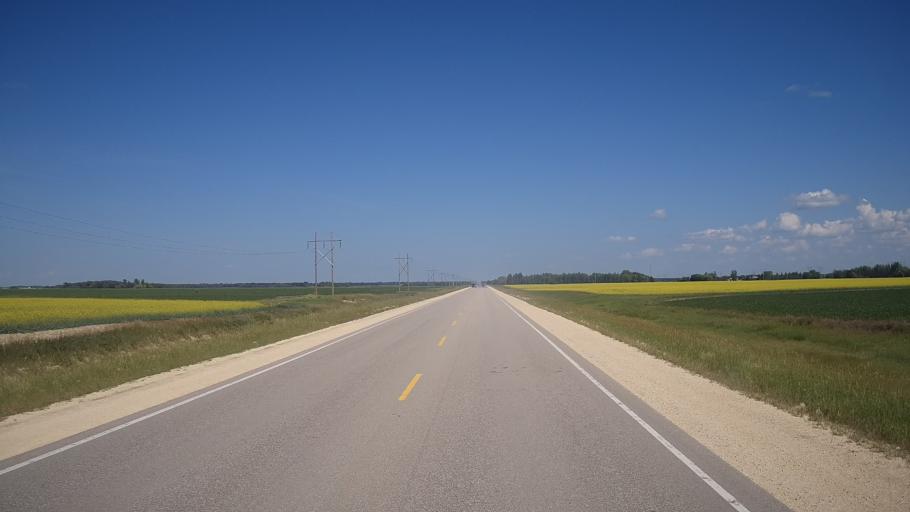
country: CA
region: Manitoba
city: Stonewall
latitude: 50.1227
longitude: -97.4042
